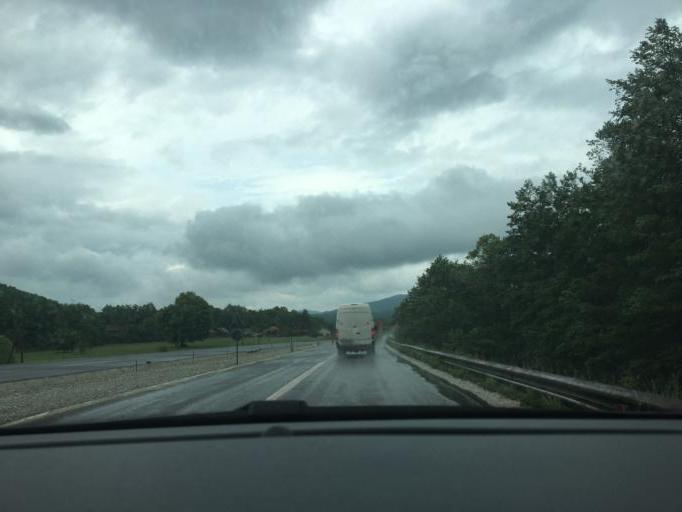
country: MK
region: Debarca
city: Belcista
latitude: 41.3276
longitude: 20.7955
